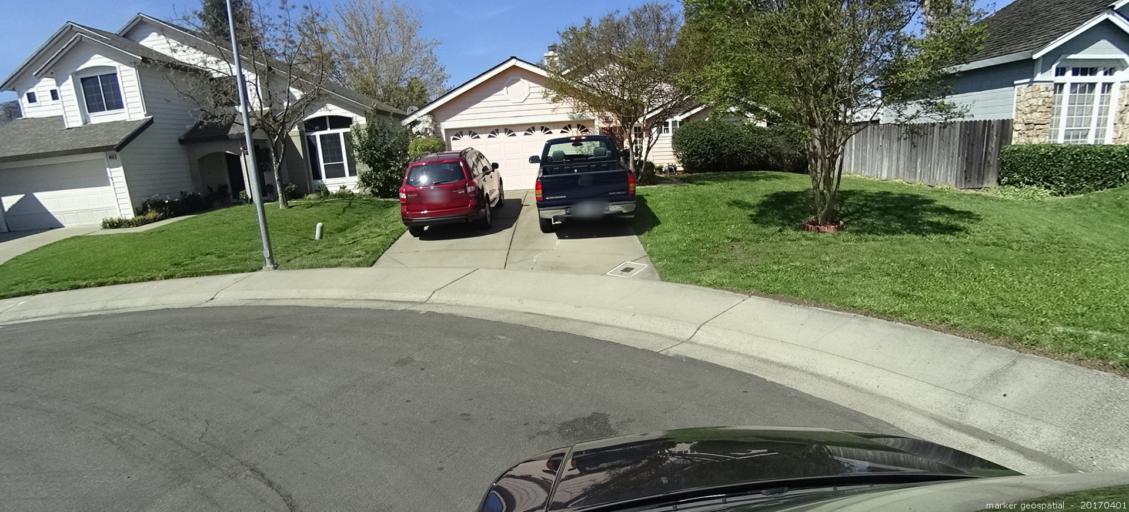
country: US
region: California
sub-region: Sacramento County
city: Laguna
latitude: 38.4494
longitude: -121.4367
